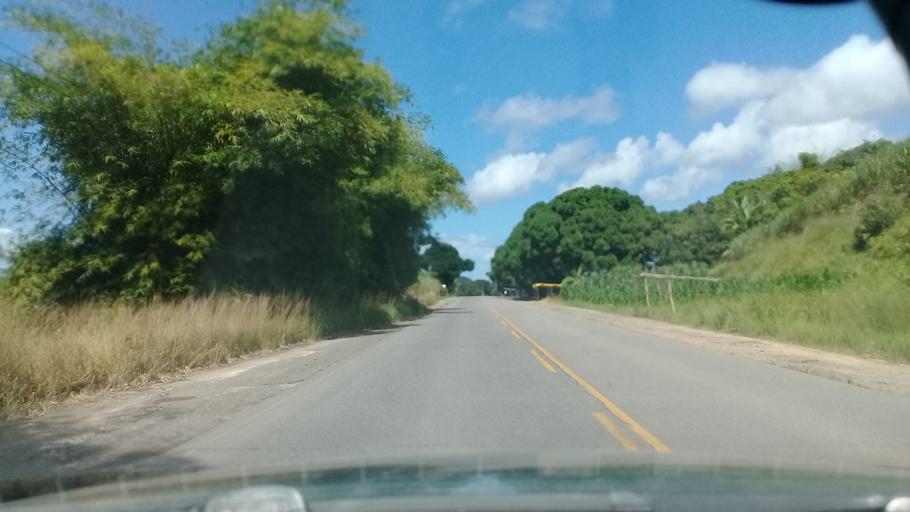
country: BR
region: Pernambuco
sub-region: Sirinhaem
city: Sirinhaem
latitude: -8.5429
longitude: -35.0878
